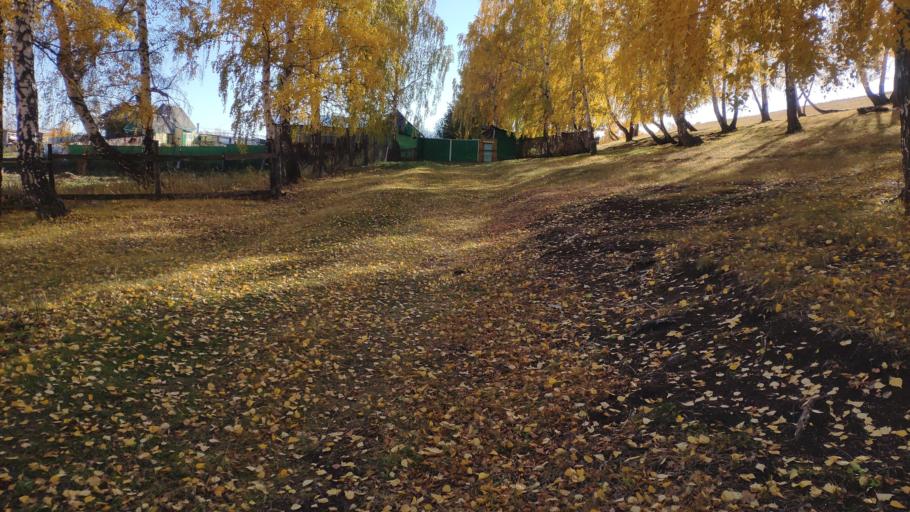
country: RU
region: Bashkortostan
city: Abzakovo
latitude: 53.3433
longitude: 58.5028
